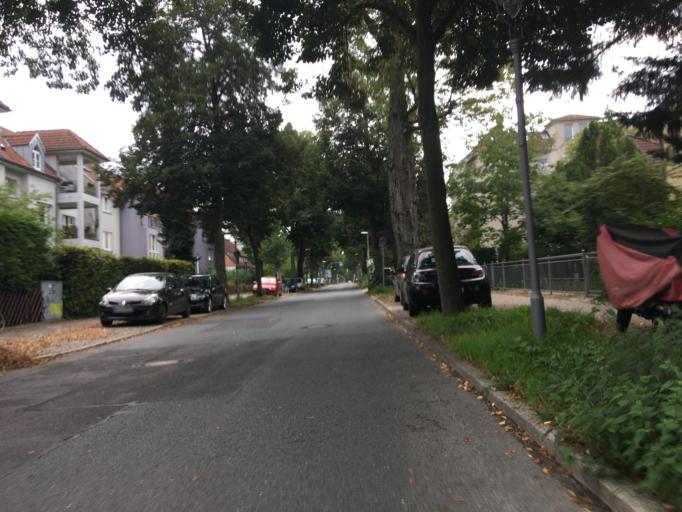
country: DE
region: Berlin
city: Lichterfelde
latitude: 52.4153
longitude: 13.3253
